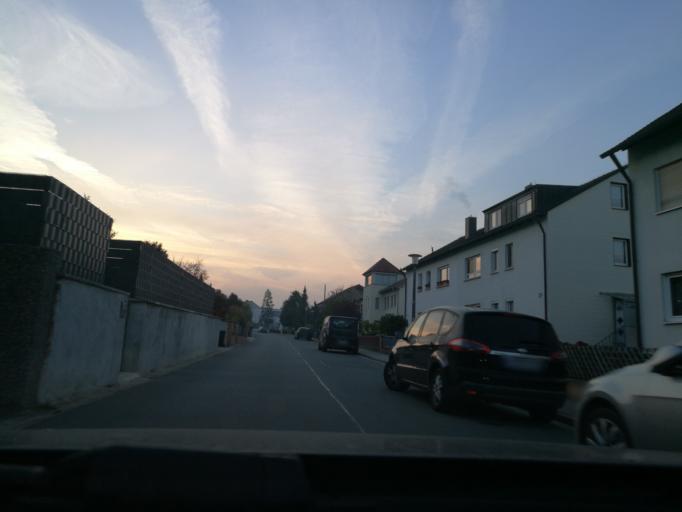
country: DE
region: Bavaria
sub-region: Regierungsbezirk Mittelfranken
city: Veitsbronn
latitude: 49.5107
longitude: 10.8901
